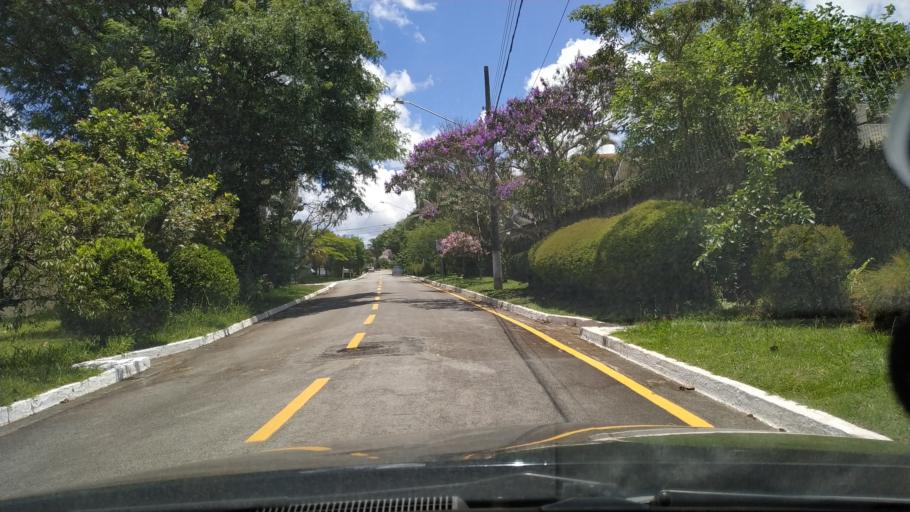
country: BR
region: Sao Paulo
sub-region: Santana De Parnaiba
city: Santana de Parnaiba
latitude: -23.4522
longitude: -46.8817
